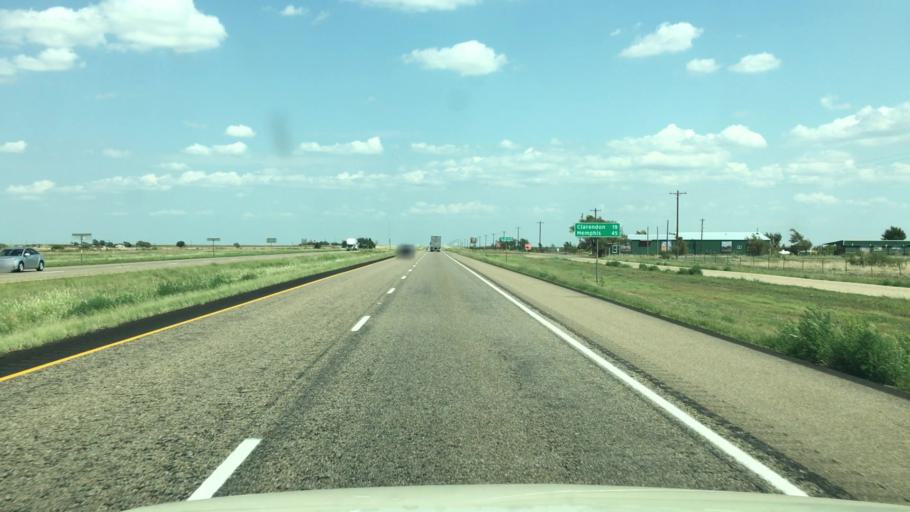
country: US
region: Texas
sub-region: Armstrong County
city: Claude
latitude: 35.0339
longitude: -101.1848
